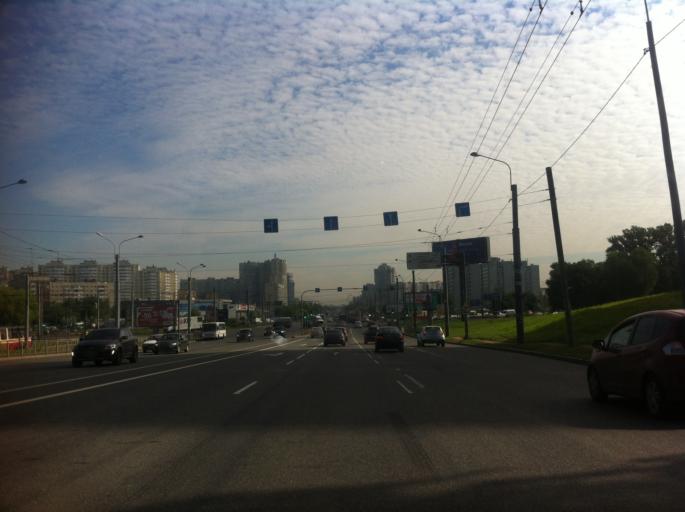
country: RU
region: St.-Petersburg
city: Uritsk
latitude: 59.8444
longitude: 30.2106
